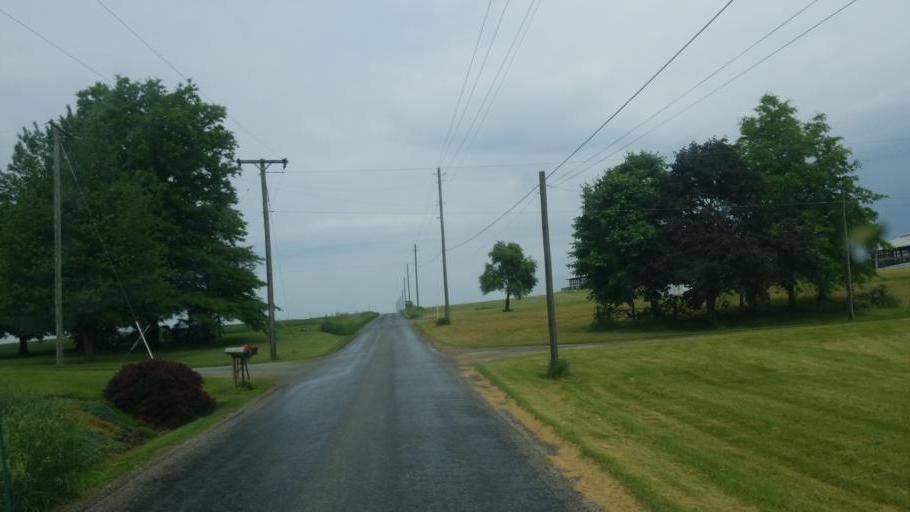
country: US
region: Ohio
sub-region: Wayne County
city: Dalton
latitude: 40.8082
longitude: -81.7258
